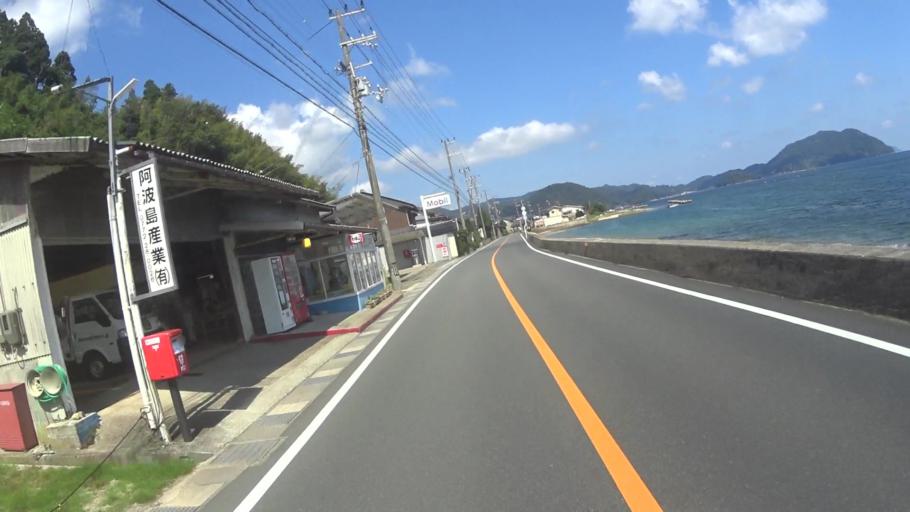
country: JP
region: Kyoto
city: Miyazu
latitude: 35.6534
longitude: 135.2563
